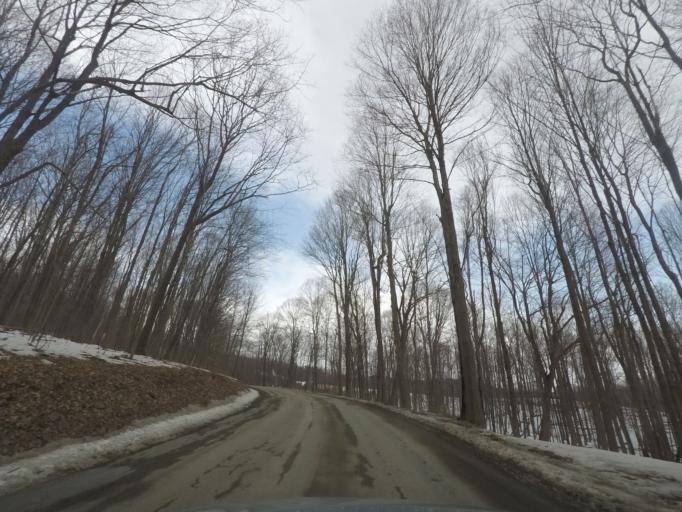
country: US
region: New York
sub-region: Saratoga County
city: Waterford
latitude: 42.7771
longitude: -73.6250
